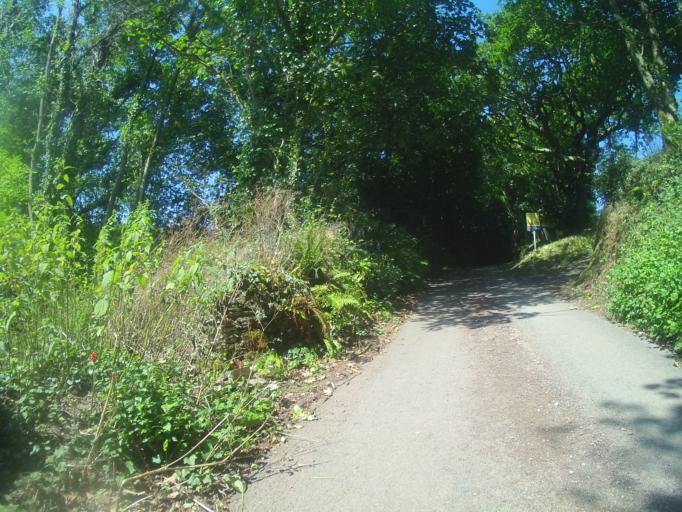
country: GB
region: England
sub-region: Devon
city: Dartmouth
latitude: 50.3602
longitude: -3.6187
